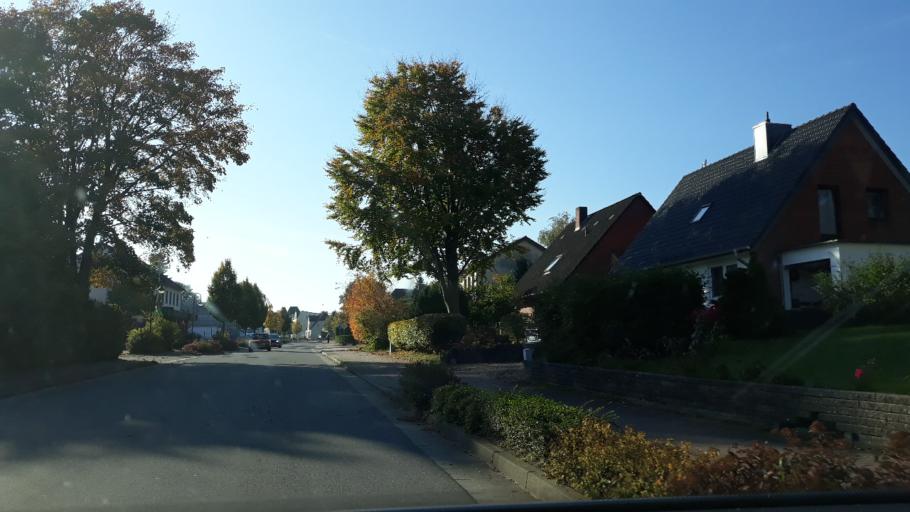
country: DE
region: Schleswig-Holstein
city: Boklund
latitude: 54.6059
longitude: 9.5838
